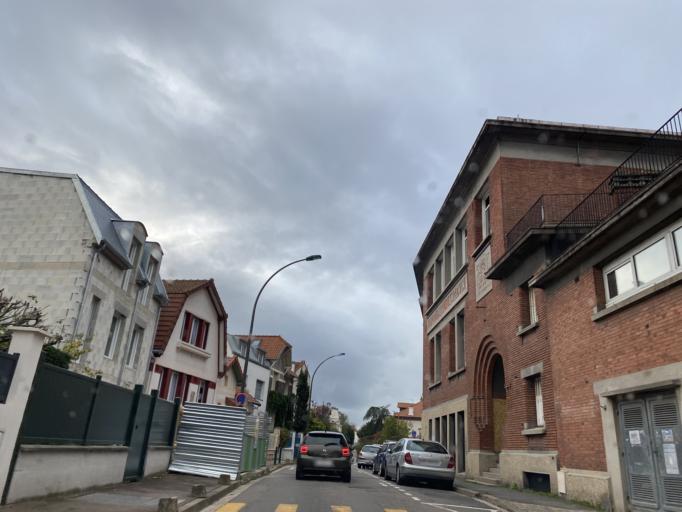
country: FR
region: Ile-de-France
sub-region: Departement des Hauts-de-Seine
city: Suresnes
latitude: 48.8769
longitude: 2.2236
